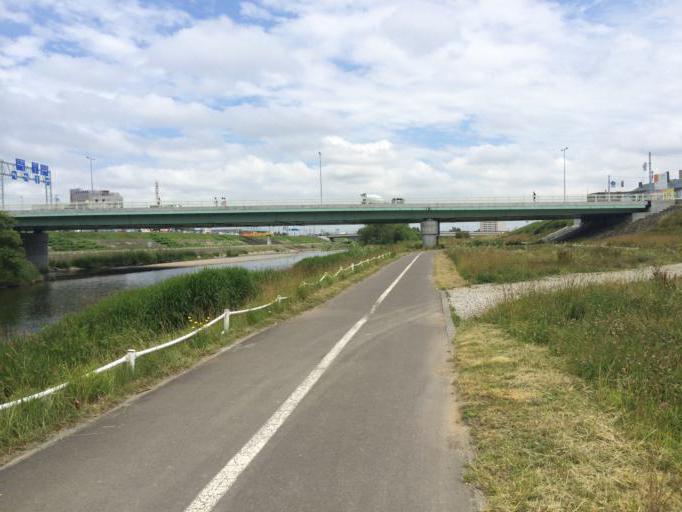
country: JP
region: Hokkaido
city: Sapporo
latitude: 43.0646
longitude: 141.3792
